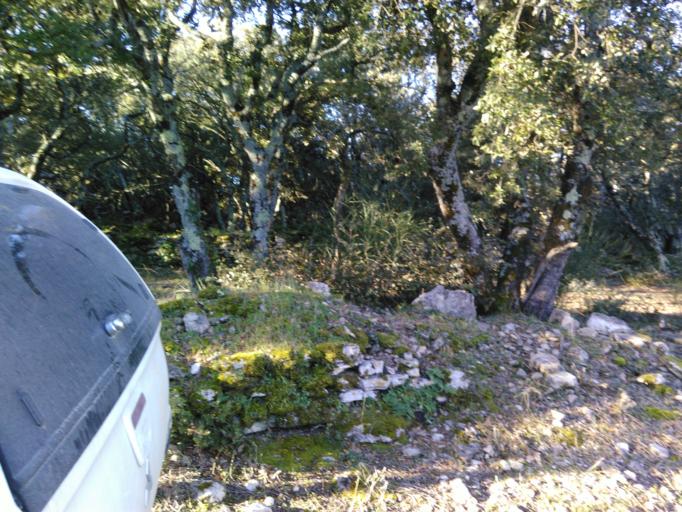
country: FR
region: Provence-Alpes-Cote d'Azur
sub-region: Departement du Vaucluse
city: Venasque
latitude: 43.9745
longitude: 5.1512
